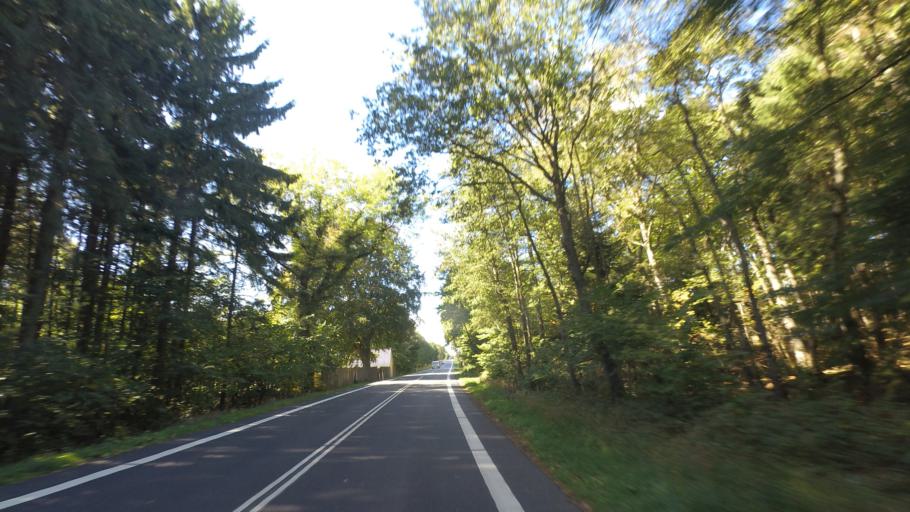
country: DK
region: Capital Region
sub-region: Bornholm Kommune
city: Akirkeby
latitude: 55.0650
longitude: 15.0147
